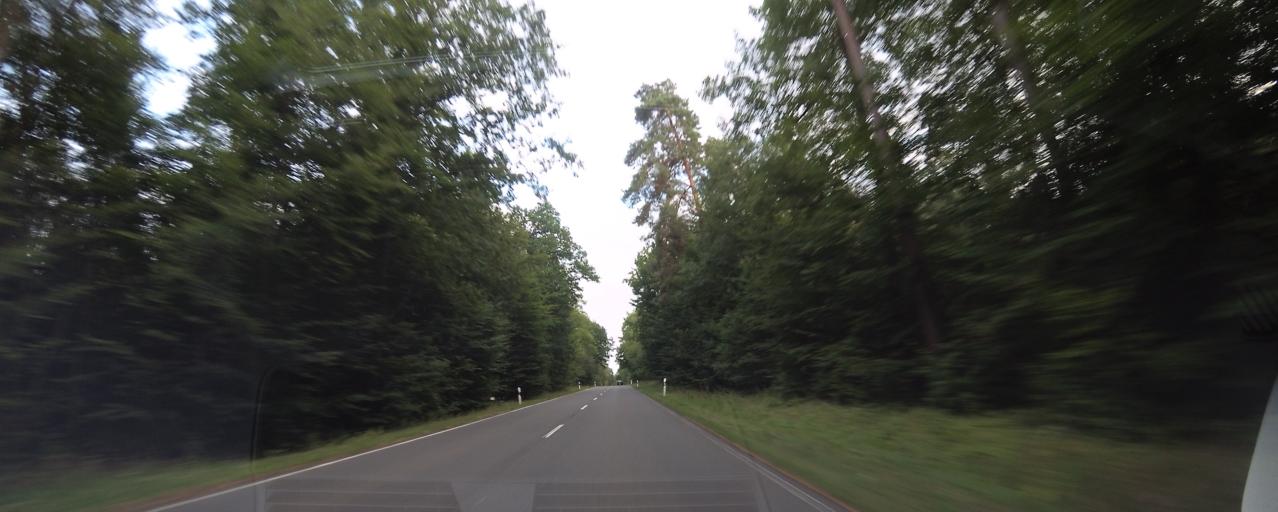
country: DE
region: Rheinland-Pfalz
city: Zemmer
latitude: 49.9203
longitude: 6.7050
